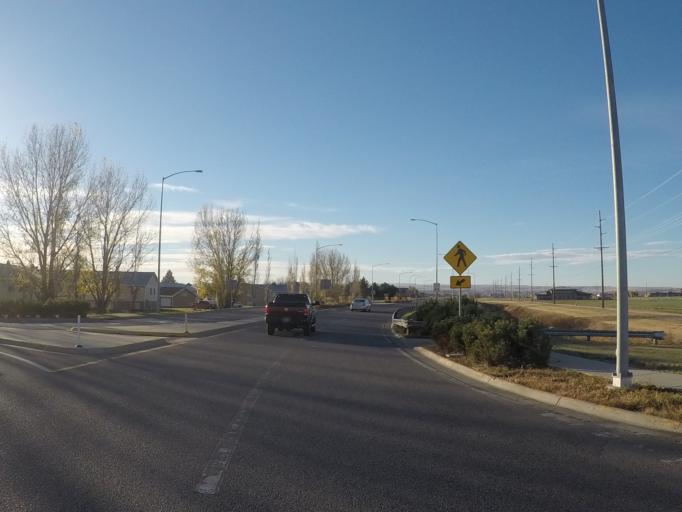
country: US
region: Montana
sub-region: Yellowstone County
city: Billings
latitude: 45.7623
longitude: -108.6178
